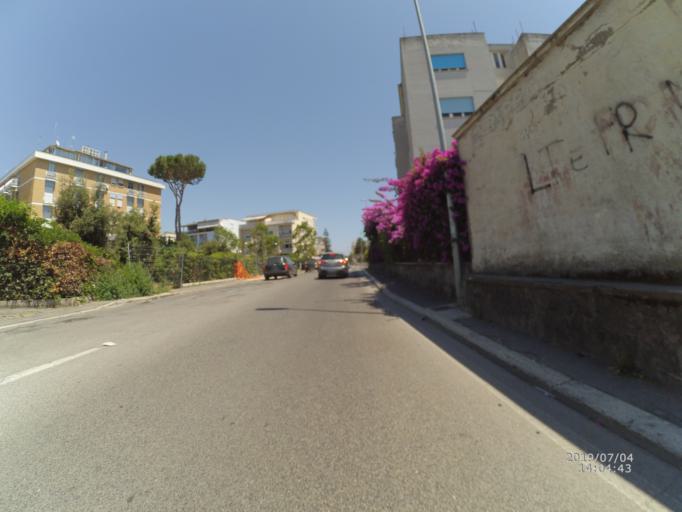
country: IT
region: Latium
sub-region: Provincia di Latina
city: Terracina
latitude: 41.2855
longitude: 13.2473
